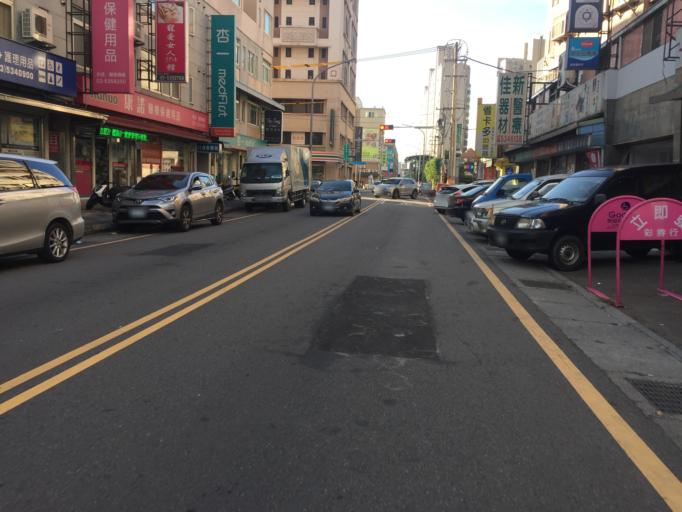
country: TW
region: Taiwan
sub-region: Hsinchu
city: Hsinchu
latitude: 24.8150
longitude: 120.9807
